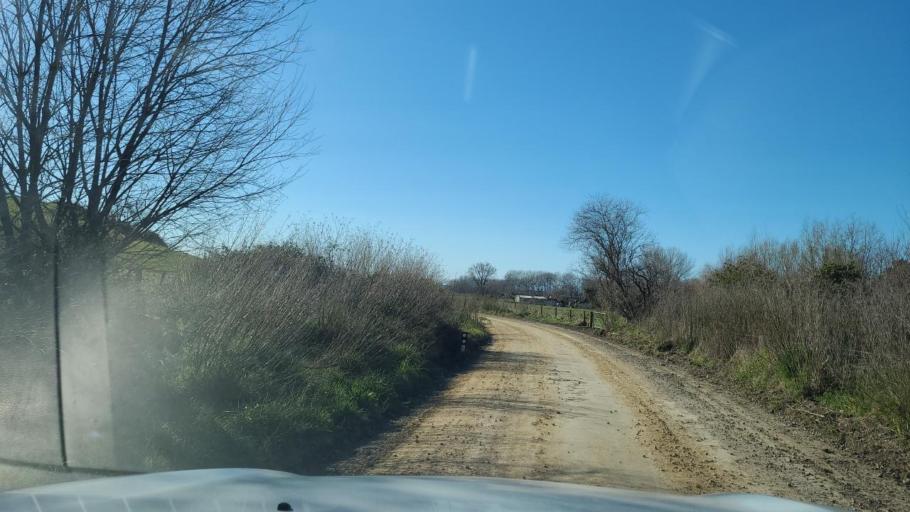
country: NZ
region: Hawke's Bay
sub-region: Hastings District
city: Hastings
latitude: -39.8009
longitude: 176.9790
